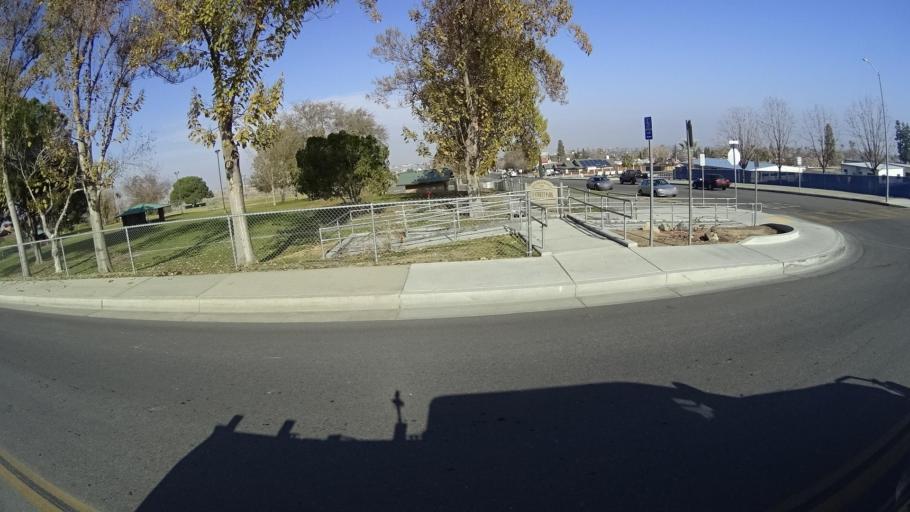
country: US
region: California
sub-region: Kern County
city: Taft Heights
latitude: 35.1369
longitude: -119.4743
